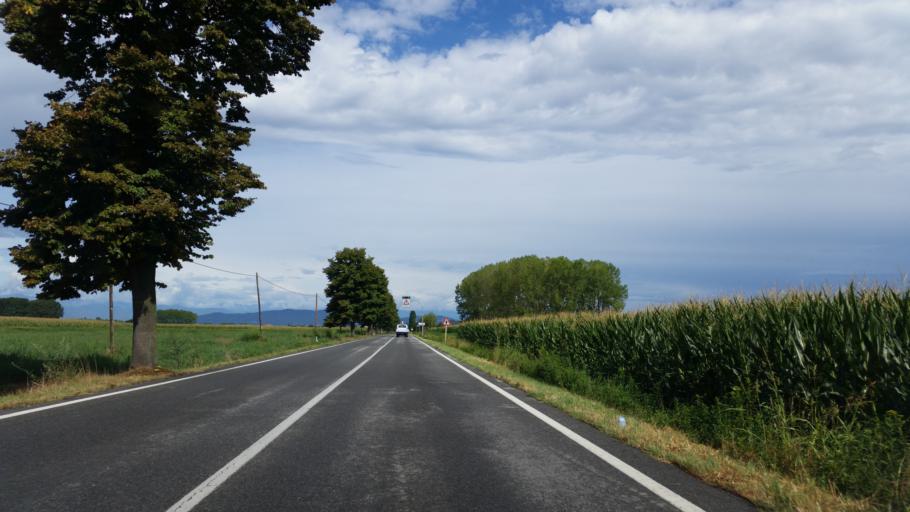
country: IT
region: Piedmont
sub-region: Provincia di Torino
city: Poirino
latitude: 44.8990
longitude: 7.8602
